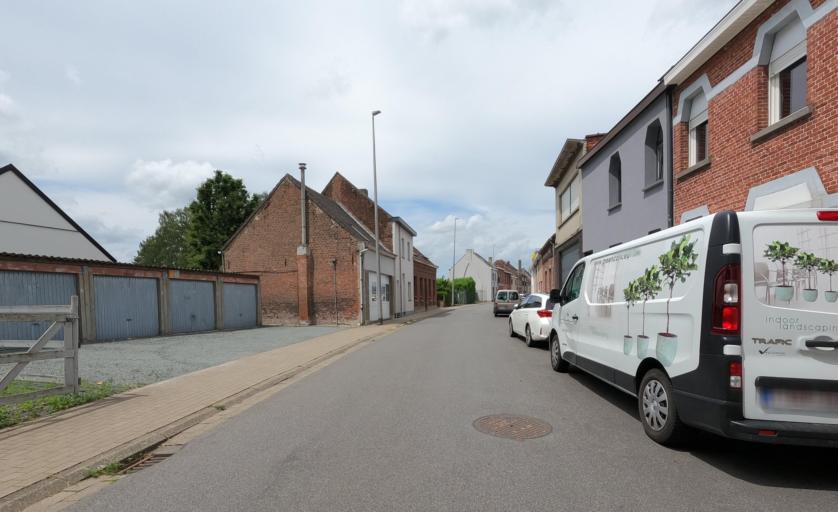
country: BE
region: Flanders
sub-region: Provincie Oost-Vlaanderen
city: Dendermonde
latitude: 51.0180
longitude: 4.0886
